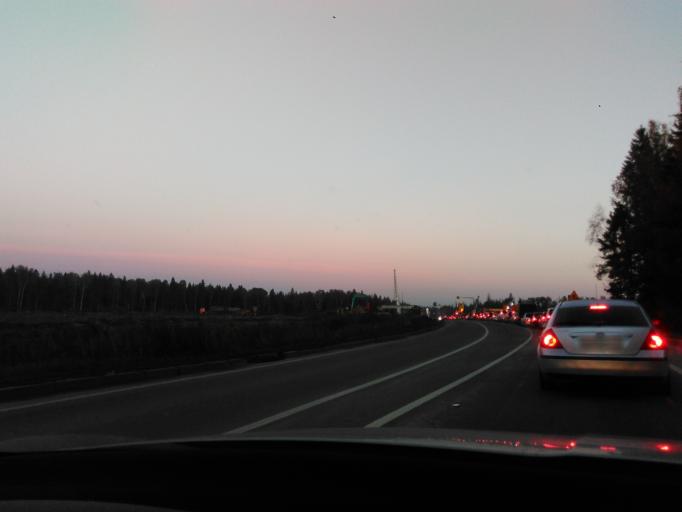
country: RU
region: Moskovskaya
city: Povarovo
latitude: 56.0079
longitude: 37.0230
